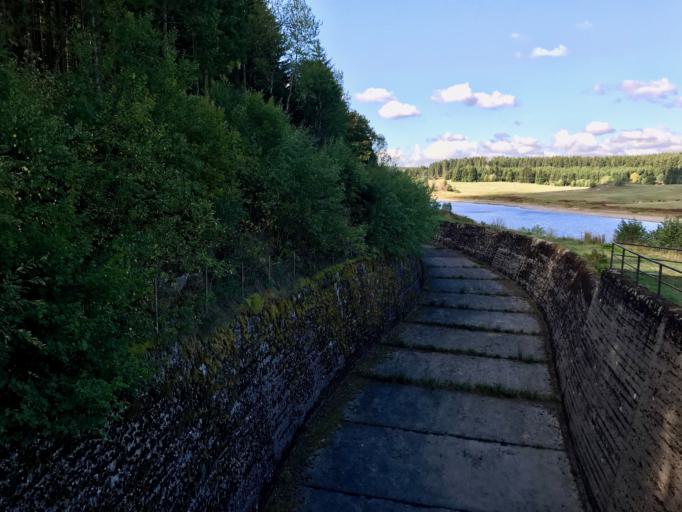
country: DE
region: Saxony-Anhalt
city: Elbingerode
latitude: 51.7468
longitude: 10.7430
